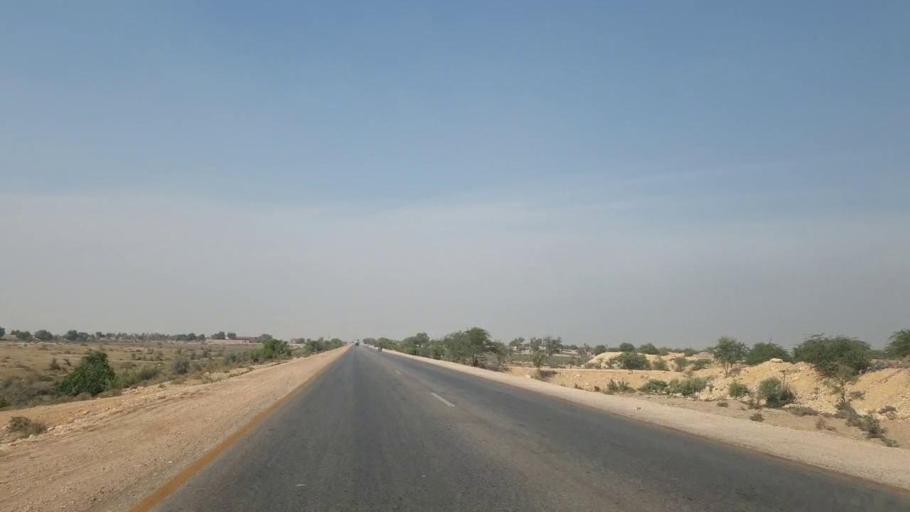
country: PK
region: Sindh
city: Hala
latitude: 25.8721
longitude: 68.2541
